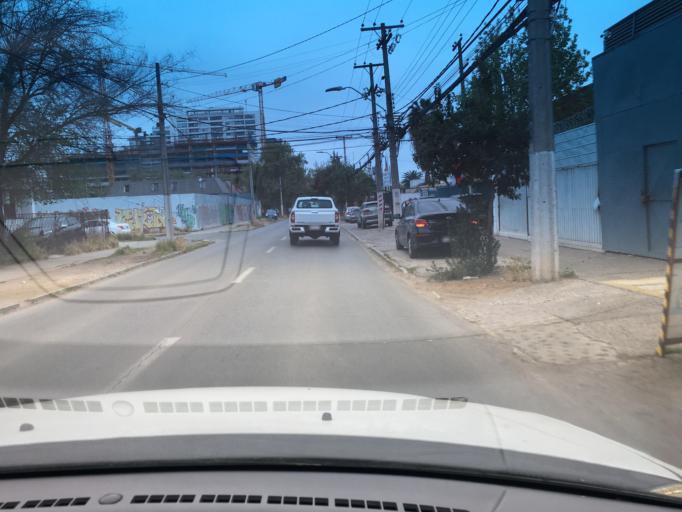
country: CL
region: Santiago Metropolitan
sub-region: Provincia de Santiago
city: Villa Presidente Frei, Nunoa, Santiago, Chile
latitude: -33.4804
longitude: -70.6015
